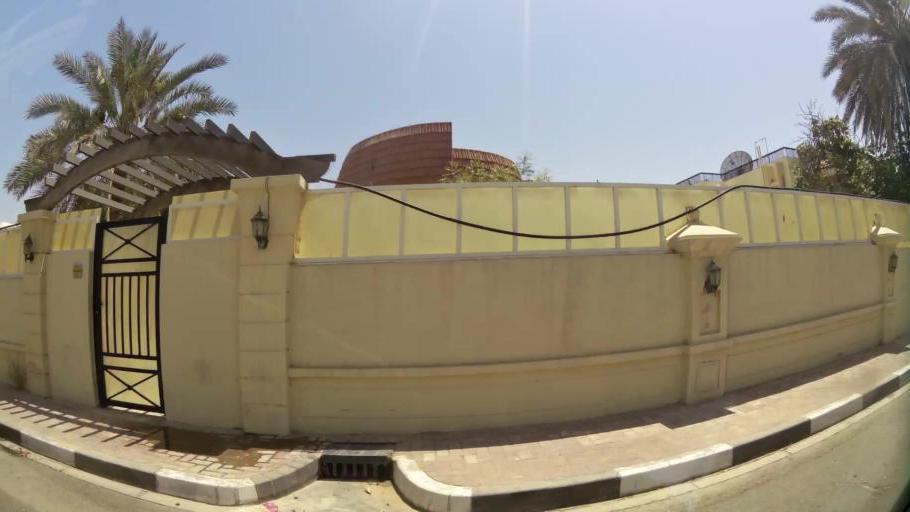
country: AE
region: Ash Shariqah
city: Sharjah
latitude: 25.2933
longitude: 55.3438
